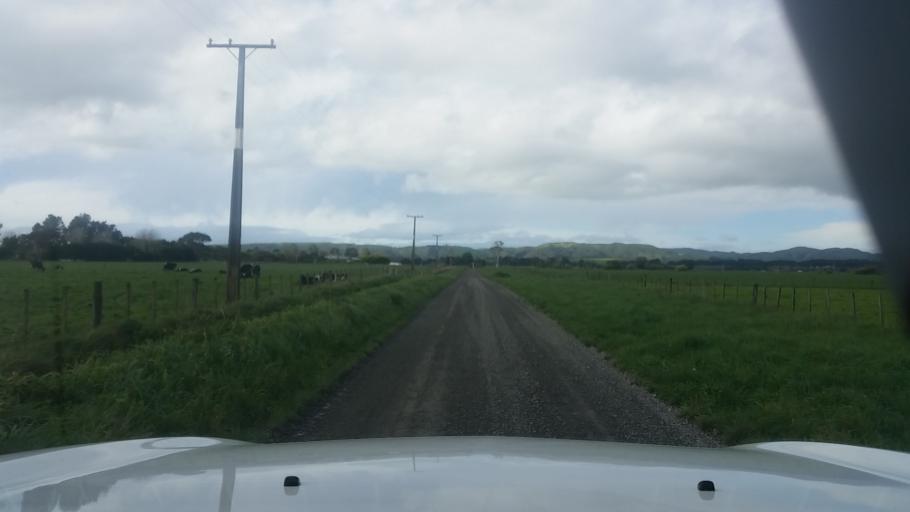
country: NZ
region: Wellington
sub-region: South Wairarapa District
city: Waipawa
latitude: -41.1431
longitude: 175.4154
